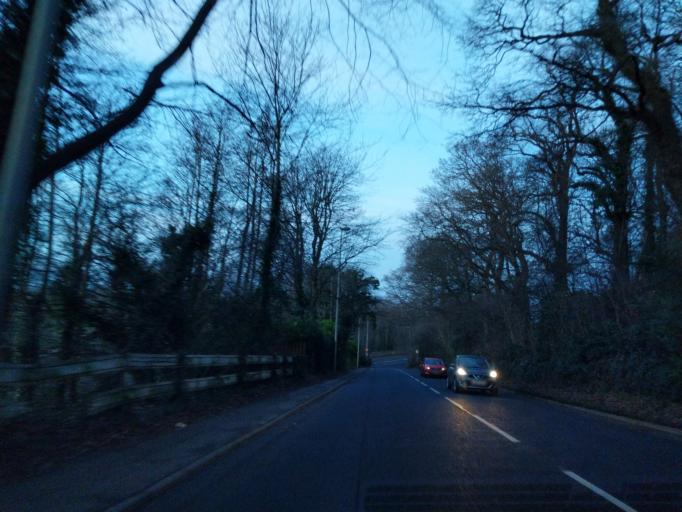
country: GB
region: Scotland
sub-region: Midlothian
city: Bonnyrigg
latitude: 55.8830
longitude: -3.1114
